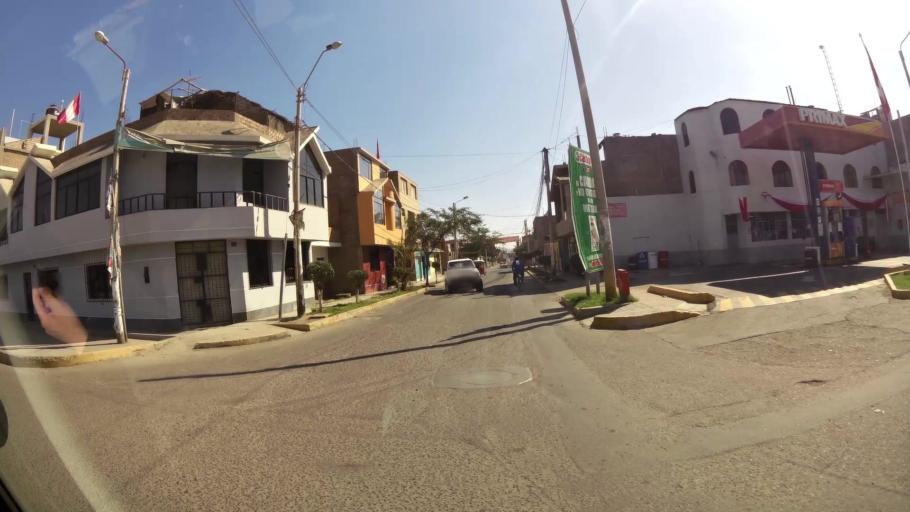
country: PE
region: Ica
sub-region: Provincia de Ica
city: La Tinguina
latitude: -14.0364
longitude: -75.7071
